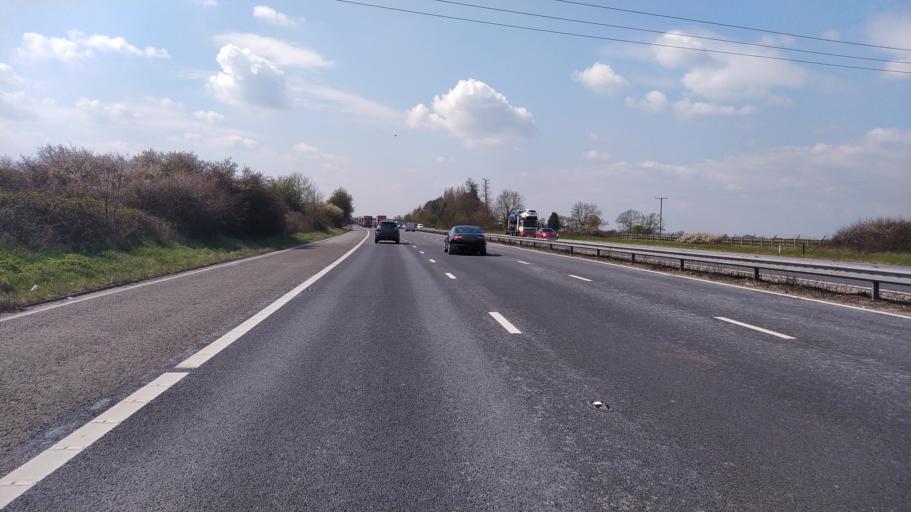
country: GB
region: England
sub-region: Wiltshire
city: Lyneham
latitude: 51.5430
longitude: -1.9772
